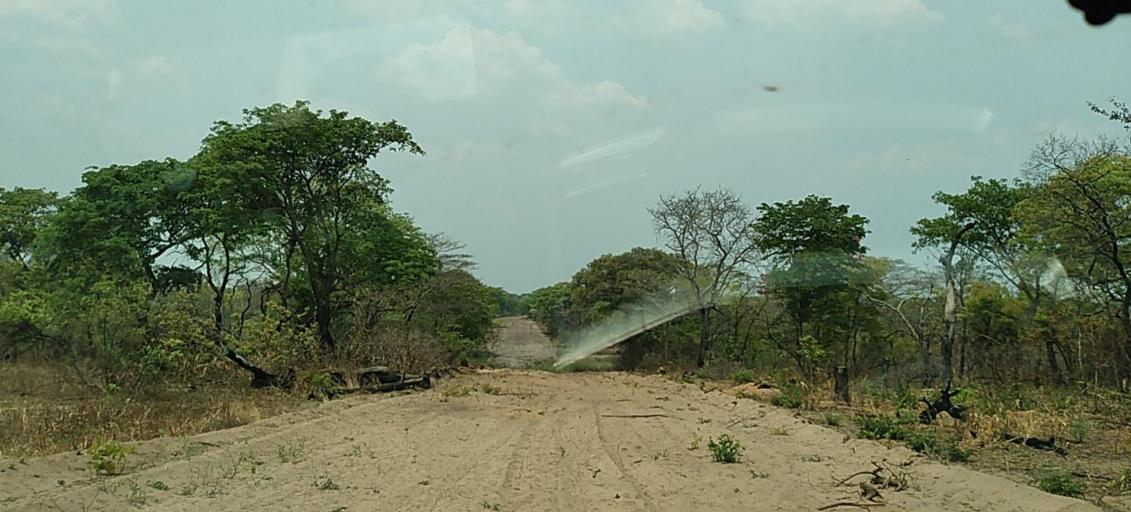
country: ZM
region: Western
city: Lukulu
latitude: -14.0034
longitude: 23.5879
